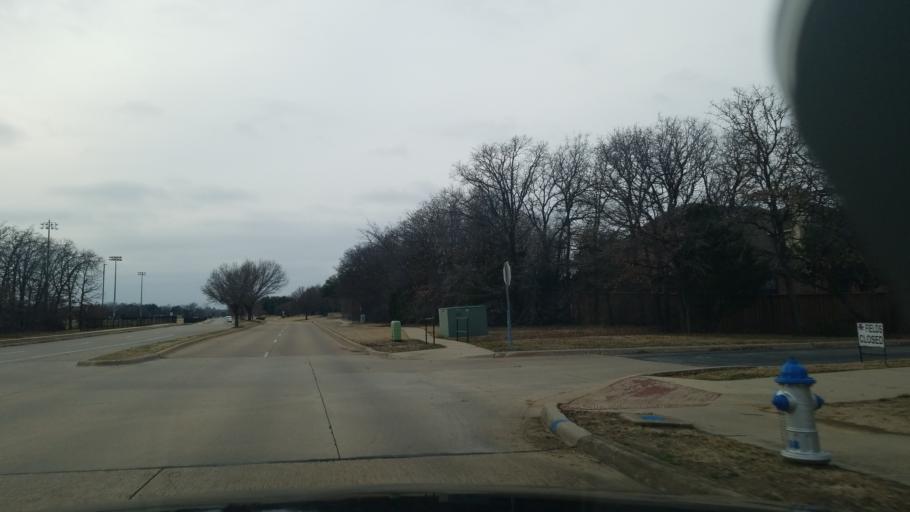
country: US
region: Texas
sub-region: Denton County
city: Corinth
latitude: 33.1534
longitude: -97.0466
